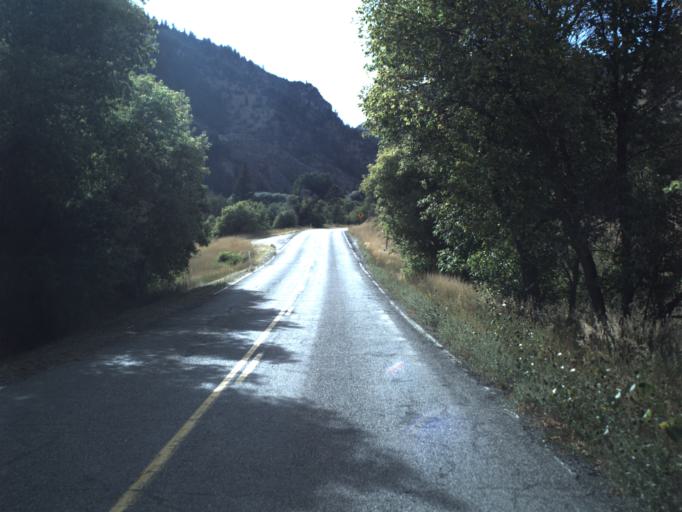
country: US
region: Utah
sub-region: Cache County
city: Millville
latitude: 41.6276
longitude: -111.6808
